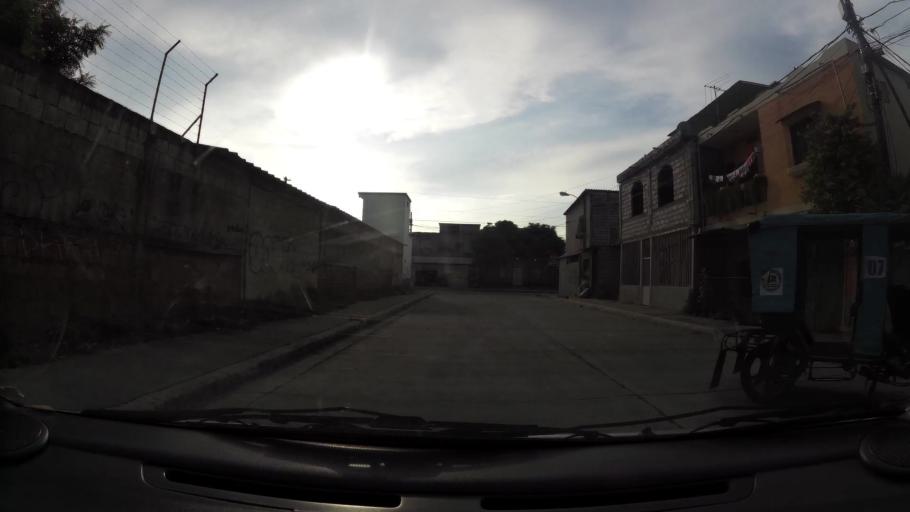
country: EC
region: Guayas
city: Eloy Alfaro
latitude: -2.0887
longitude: -79.9020
